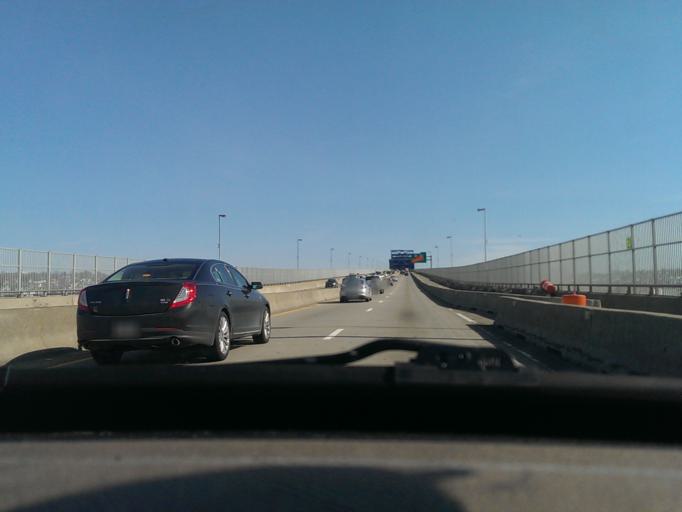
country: US
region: Massachusetts
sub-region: Bristol County
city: Fall River
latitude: 41.7120
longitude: -71.1754
